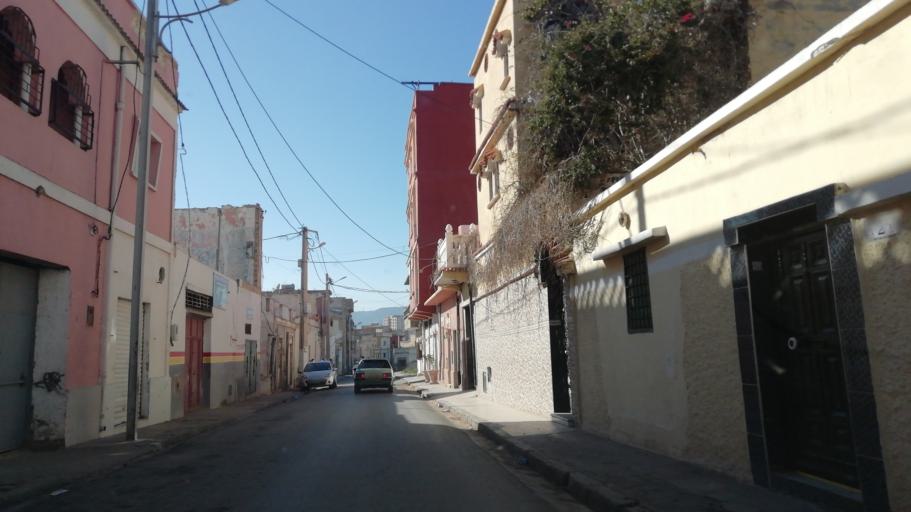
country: DZ
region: Oran
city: Oran
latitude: 35.7042
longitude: -0.6154
